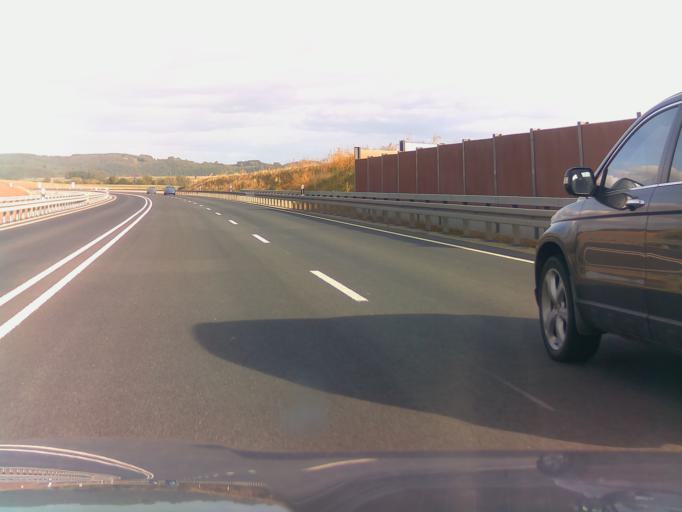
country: DE
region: Thuringia
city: Behringen
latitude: 50.7519
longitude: 11.0176
